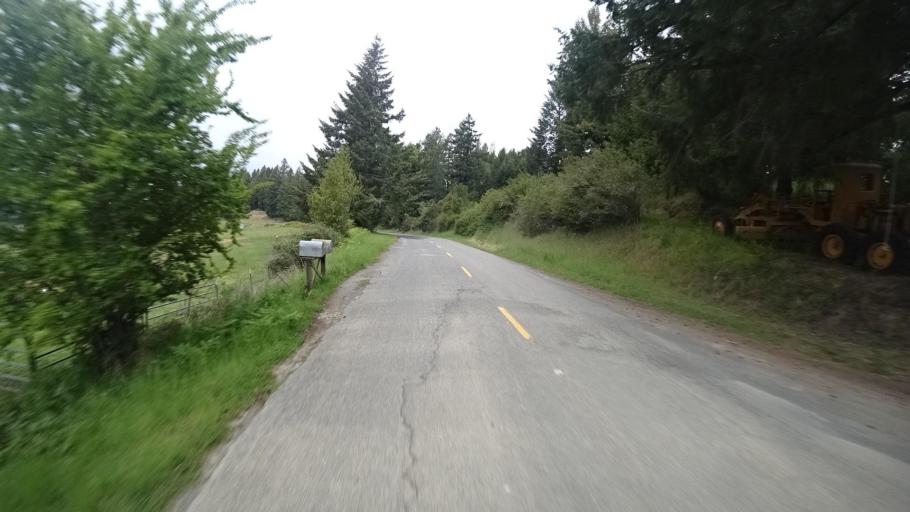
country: US
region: California
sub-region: Humboldt County
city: Redway
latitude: 40.2892
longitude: -123.8035
